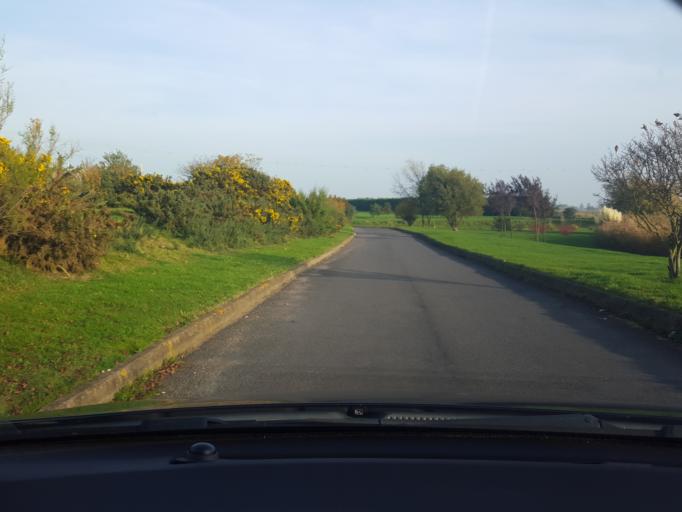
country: GB
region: England
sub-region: Essex
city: Walton-on-the-Naze
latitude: 51.8618
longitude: 1.2575
